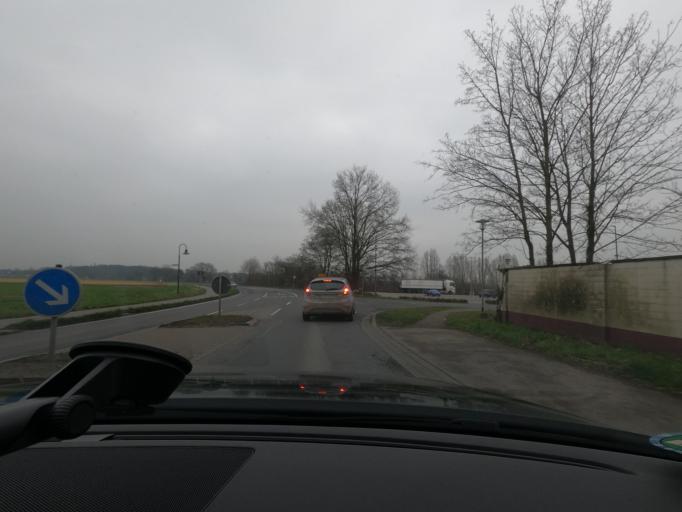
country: DE
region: North Rhine-Westphalia
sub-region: Regierungsbezirk Dusseldorf
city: Wachtendonk
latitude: 51.4016
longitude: 6.3123
